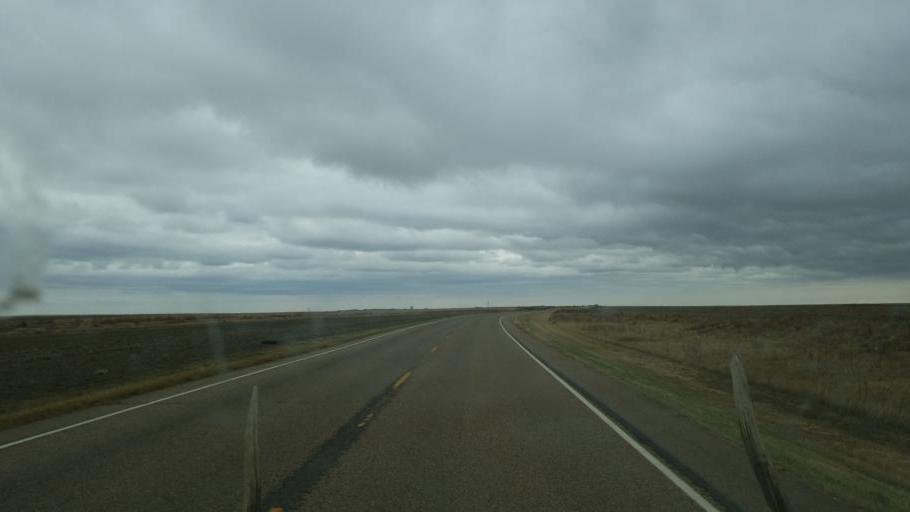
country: US
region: Colorado
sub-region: Cheyenne County
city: Cheyenne Wells
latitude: 38.8174
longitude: -102.4929
